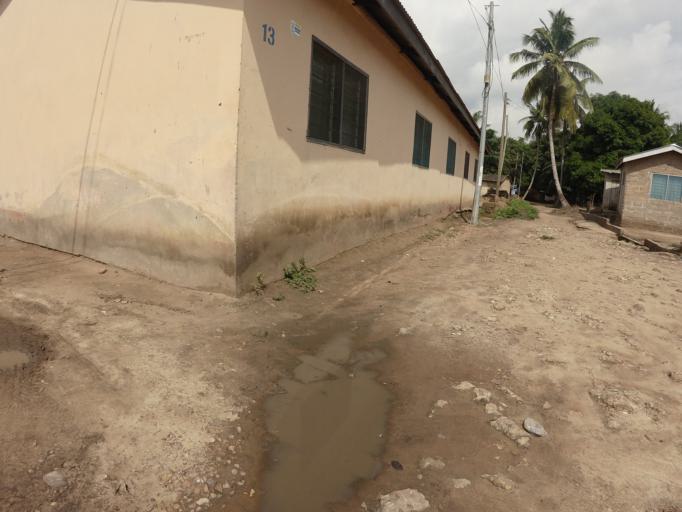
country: GH
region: Volta
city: Ho
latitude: 6.6134
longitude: 0.4773
